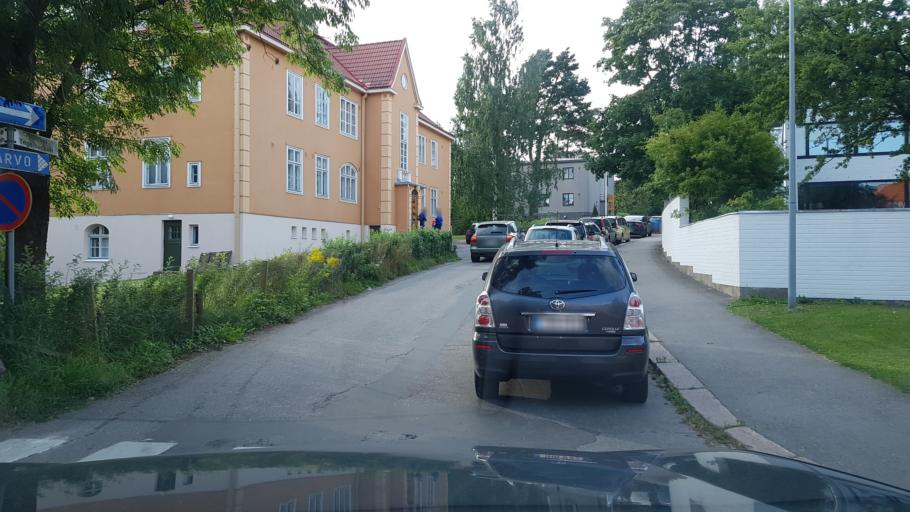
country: FI
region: Uusimaa
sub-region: Helsinki
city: Teekkarikylae
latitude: 60.1956
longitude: 24.8730
